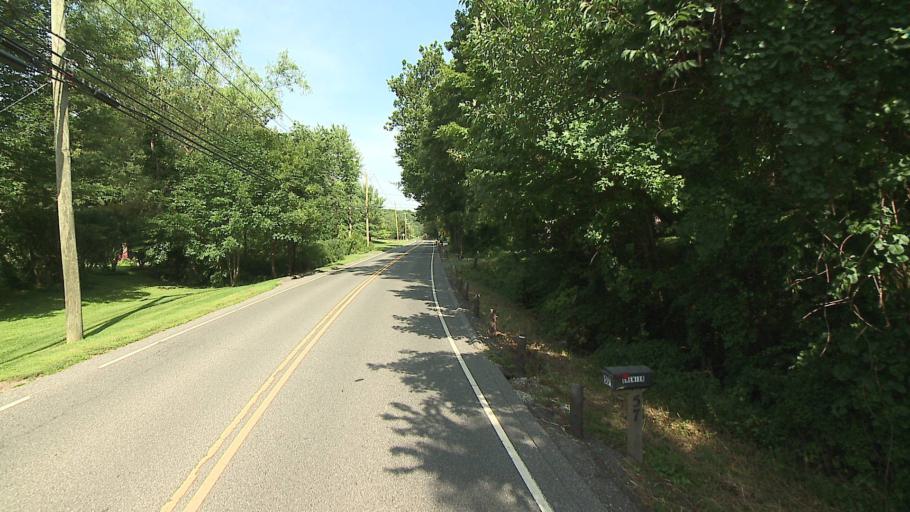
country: US
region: Connecticut
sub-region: Fairfield County
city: Sherman
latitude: 41.5910
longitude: -73.4678
